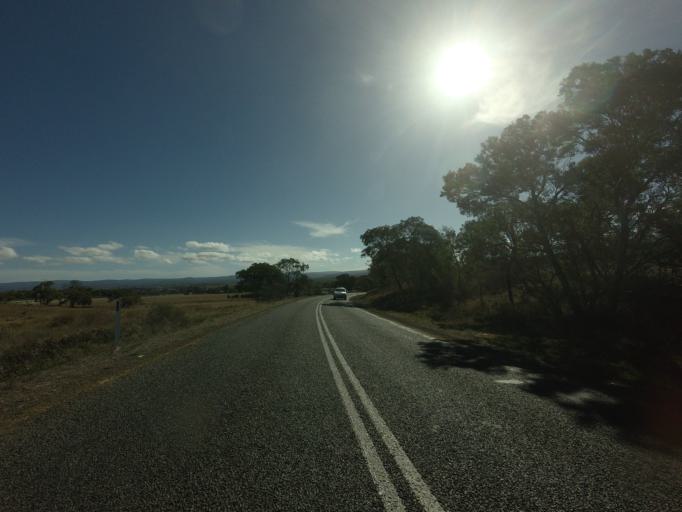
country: AU
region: Tasmania
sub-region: Break O'Day
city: St Helens
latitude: -41.9981
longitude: 148.0895
